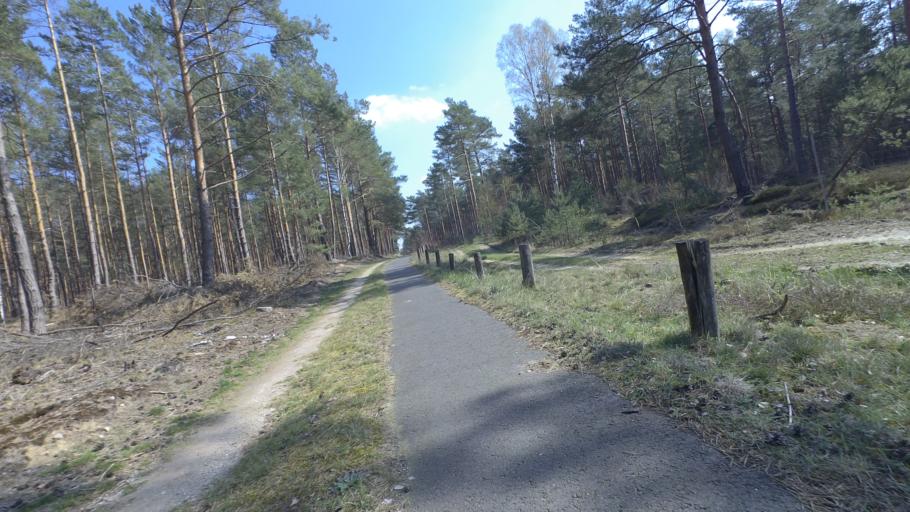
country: DE
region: Brandenburg
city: Mittenwalde
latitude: 52.1885
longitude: 13.5340
